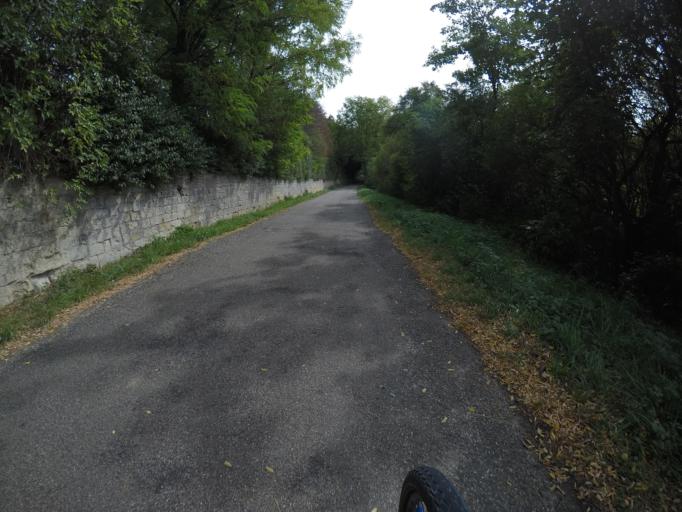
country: DE
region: Baden-Wuerttemberg
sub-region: Karlsruhe Region
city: Oberderdingen
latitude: 49.0959
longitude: 8.7579
